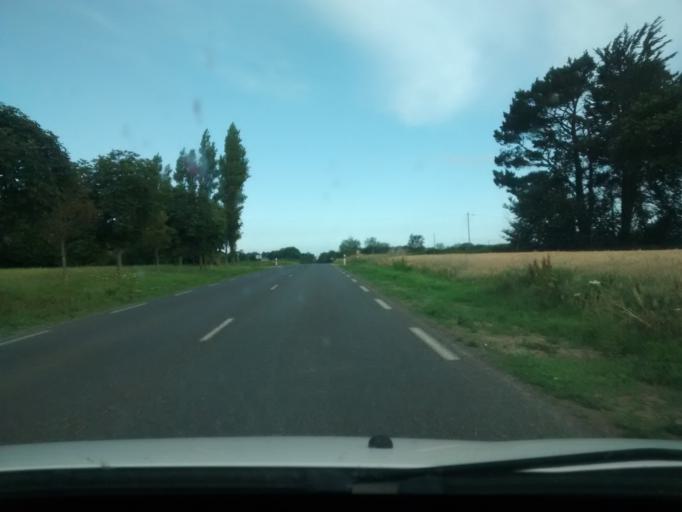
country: FR
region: Brittany
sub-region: Departement des Cotes-d'Armor
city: Trelevern
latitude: 48.7788
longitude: -3.3818
